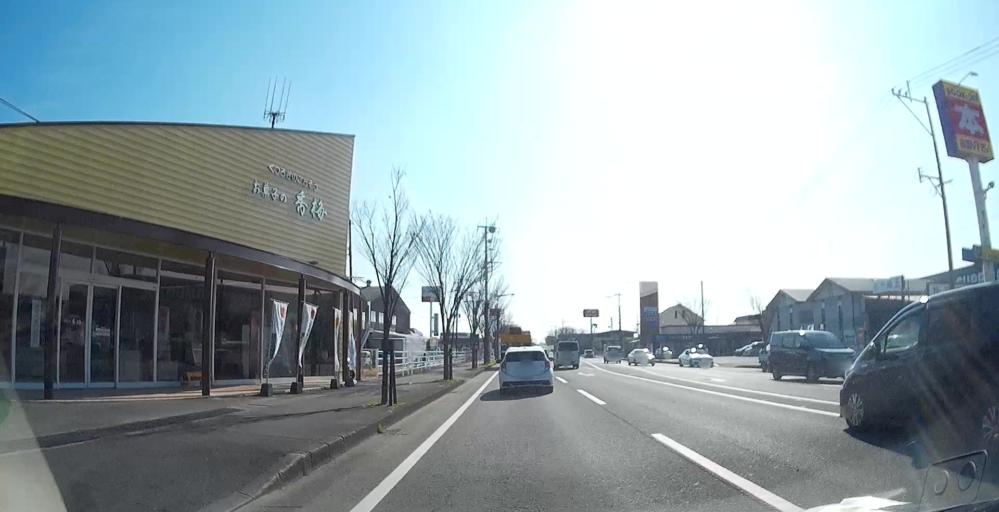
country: JP
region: Kumamoto
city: Kumamoto
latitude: 32.7827
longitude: 130.6734
